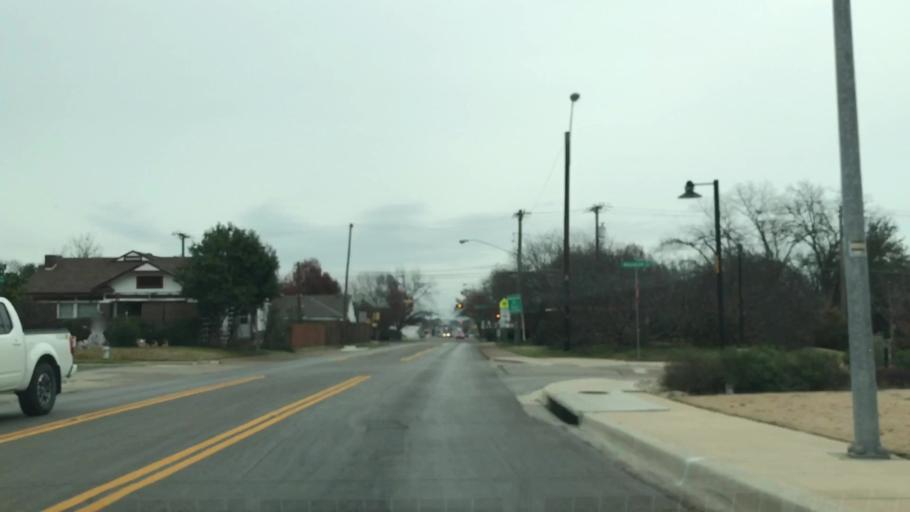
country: US
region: Texas
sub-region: Dallas County
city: Cockrell Hill
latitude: 32.7495
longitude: -96.8479
